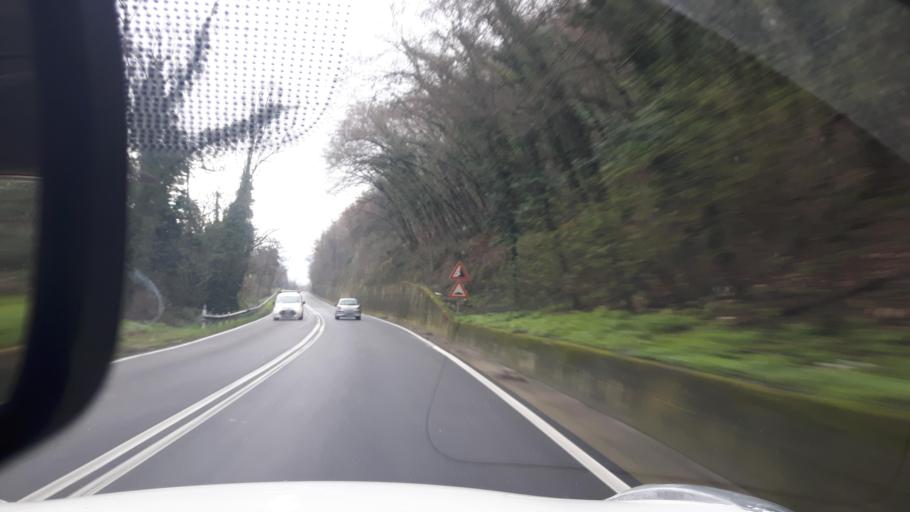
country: IT
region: Tuscany
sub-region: Province of Florence
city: Compiobbi
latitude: 43.7826
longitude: 11.3752
